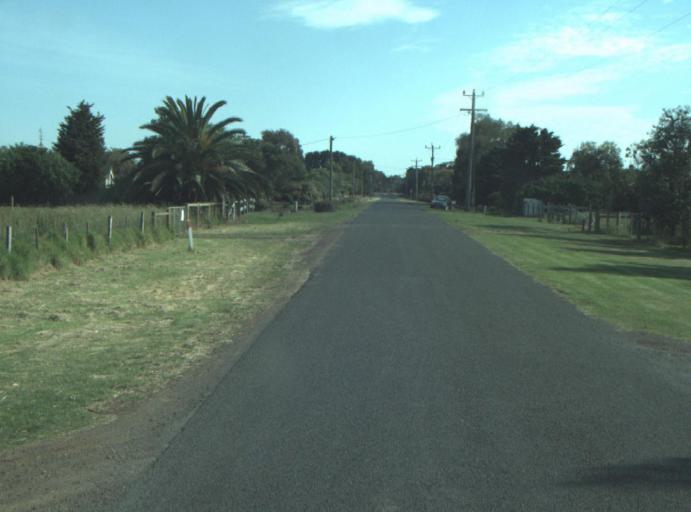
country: AU
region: Victoria
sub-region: Greater Geelong
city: Leopold
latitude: -38.1777
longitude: 144.4387
